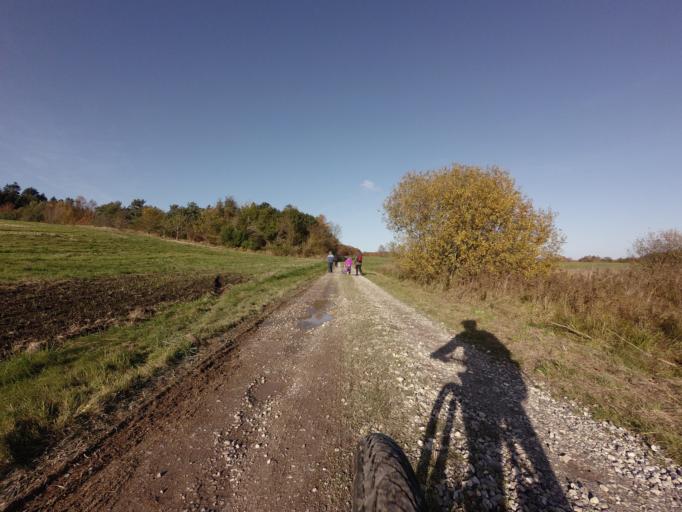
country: DK
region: Central Jutland
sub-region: Syddjurs Kommune
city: Ryomgard
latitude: 56.4417
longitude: 10.6225
